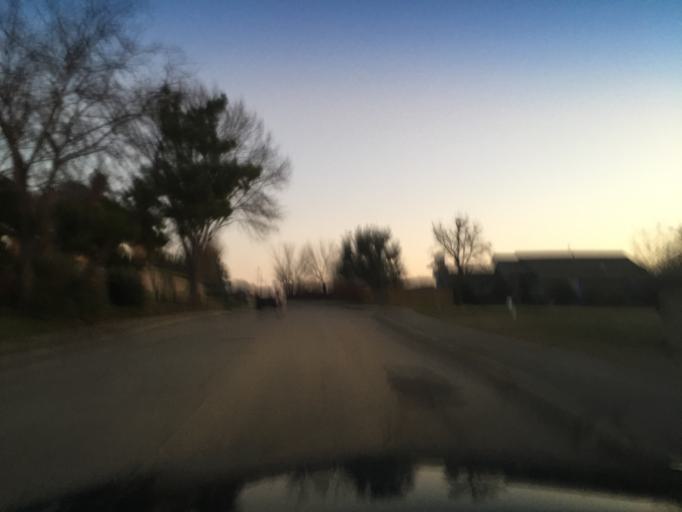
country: US
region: Texas
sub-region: Dallas County
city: Carrollton
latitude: 32.9898
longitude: -96.8986
